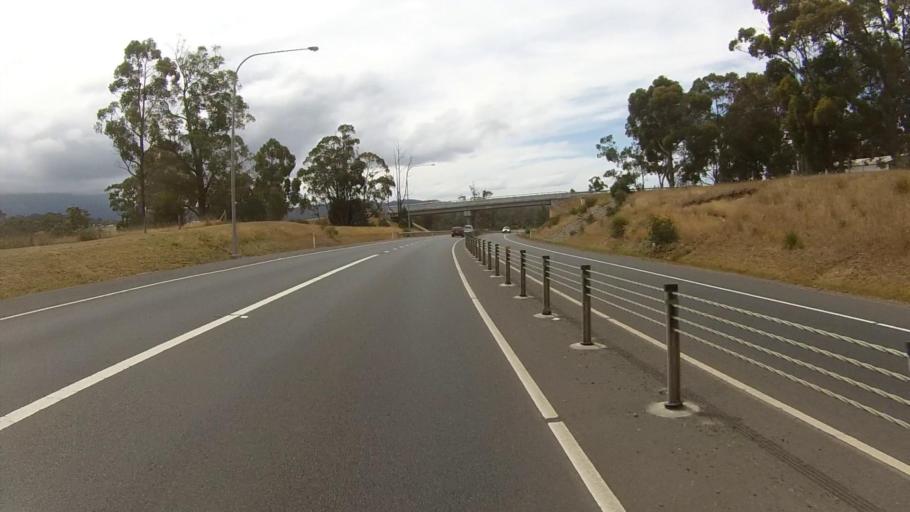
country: AU
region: Tasmania
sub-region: Kingborough
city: Kingston
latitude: -42.9845
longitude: 147.2892
